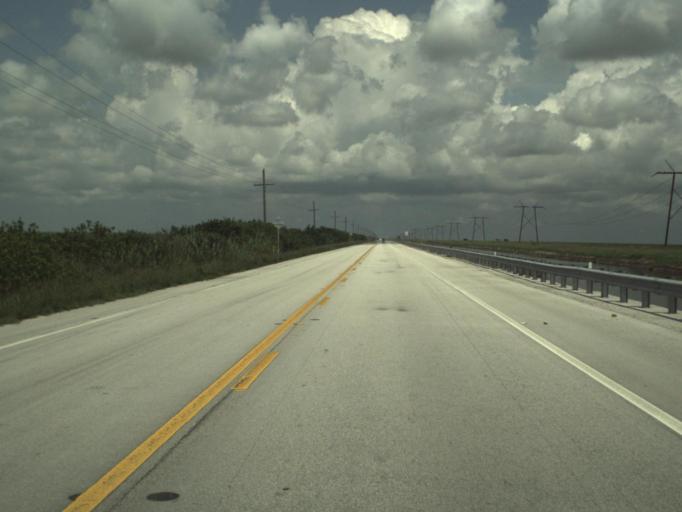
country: US
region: Florida
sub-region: Palm Beach County
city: Loxahatchee Groves
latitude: 26.7336
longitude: -80.4586
